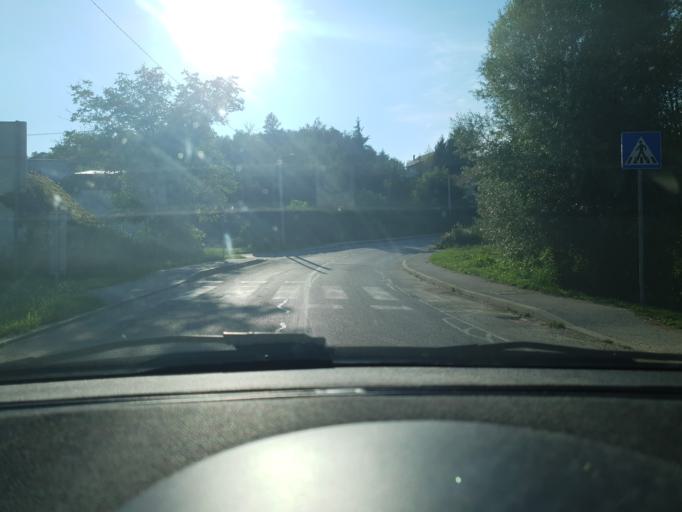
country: HR
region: Krapinsko-Zagorska
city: Radoboj
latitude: 46.1559
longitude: 15.9404
